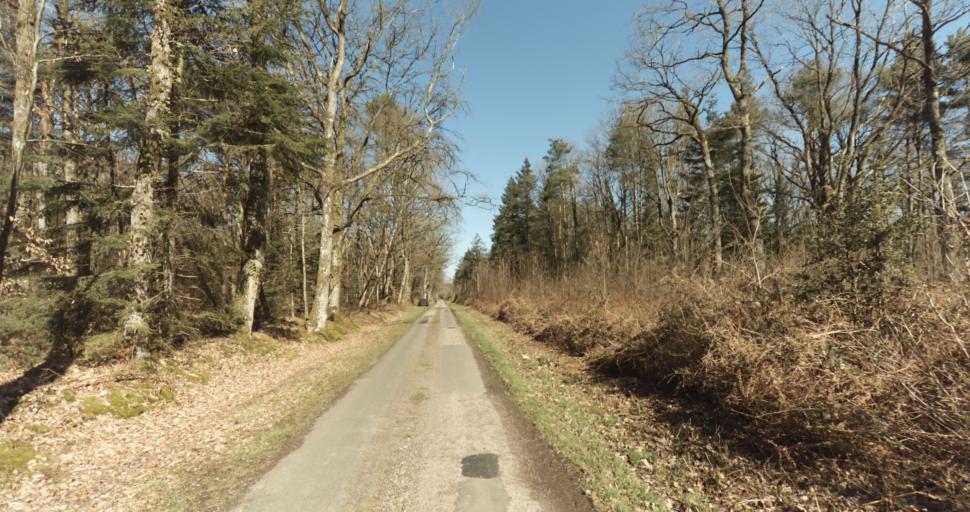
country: FR
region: Lower Normandy
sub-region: Departement du Calvados
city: Livarot
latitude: 48.9733
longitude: 0.0721
